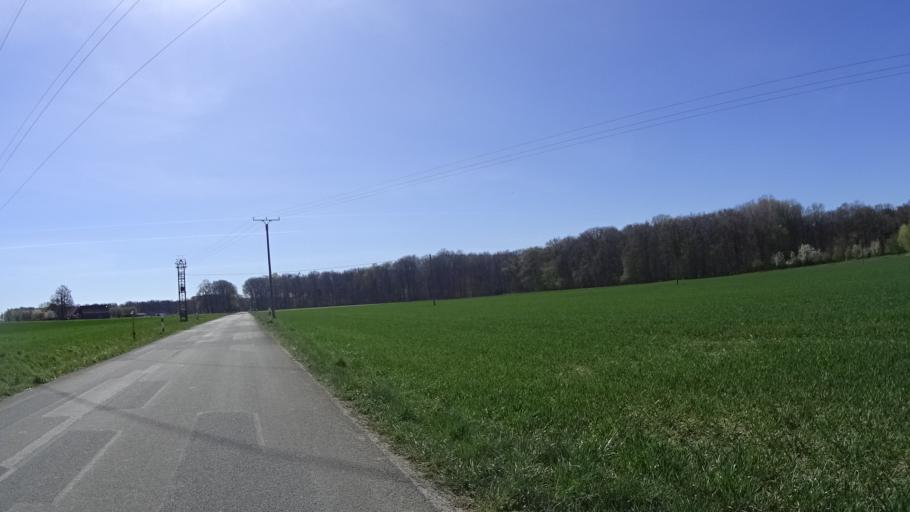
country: DE
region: North Rhine-Westphalia
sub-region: Regierungsbezirk Munster
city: Dulmen
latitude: 51.8151
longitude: 7.3499
